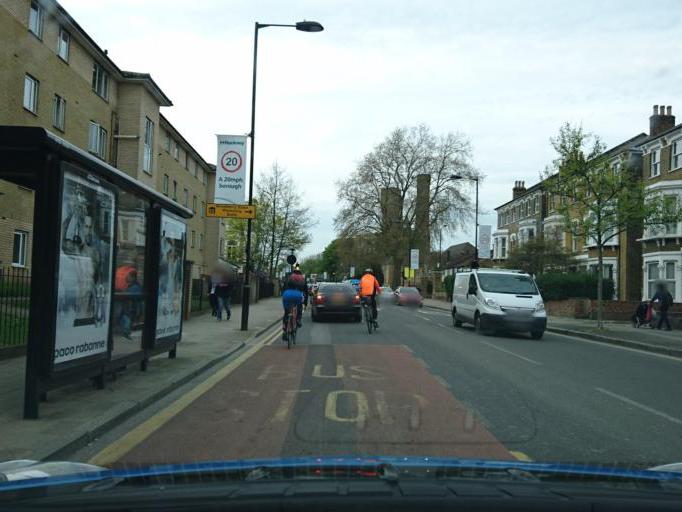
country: GB
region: England
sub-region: Greater London
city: Harringay
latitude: 51.5632
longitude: -0.0922
